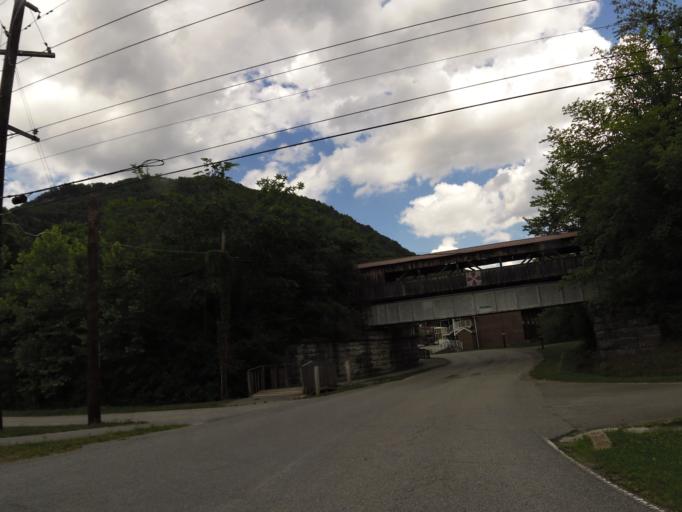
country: US
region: Tennessee
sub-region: Claiborne County
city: Harrogate
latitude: 36.5974
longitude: -83.6693
